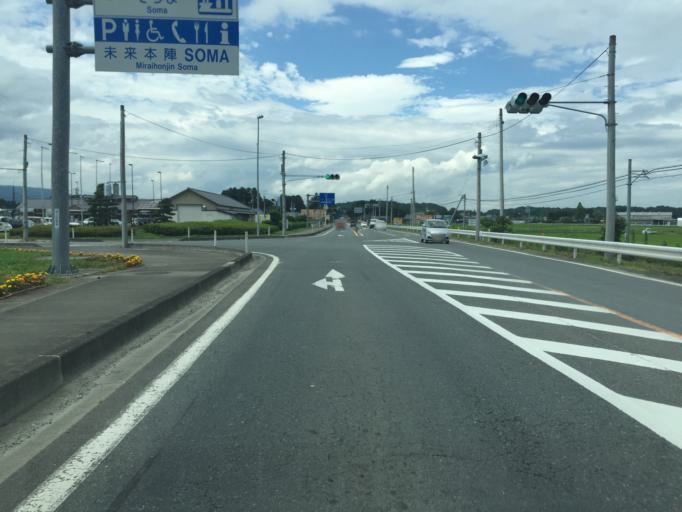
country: JP
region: Miyagi
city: Marumori
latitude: 37.7604
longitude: 140.9489
